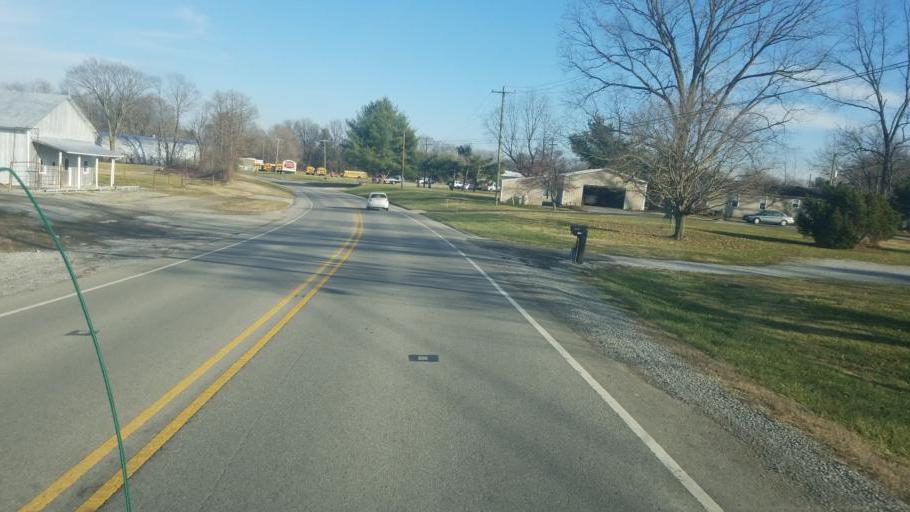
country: US
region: Illinois
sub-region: Wabash County
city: Mount Carmel
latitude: 38.4003
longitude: -87.7875
